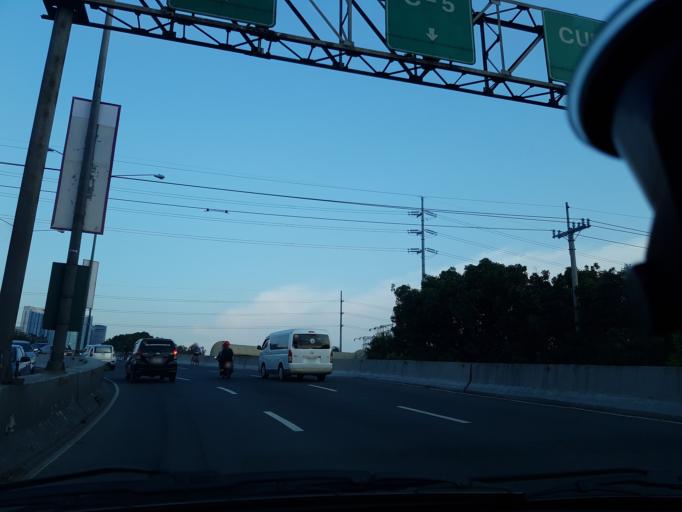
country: PH
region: Metro Manila
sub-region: Makati City
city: Makati City
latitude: 14.5556
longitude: 121.0343
